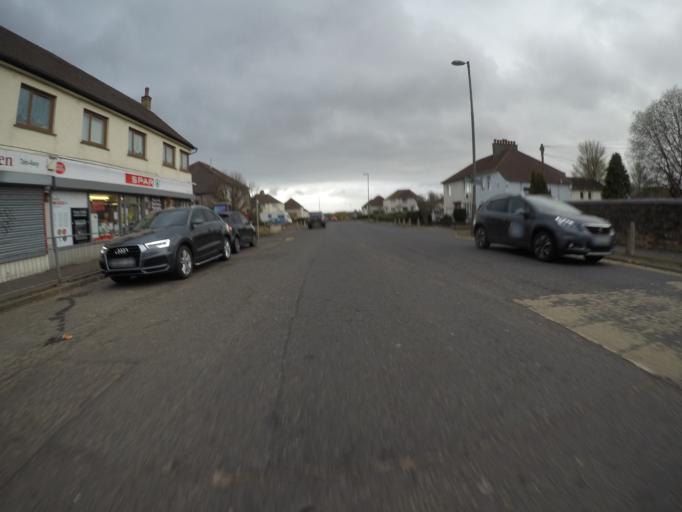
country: GB
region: Scotland
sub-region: East Ayrshire
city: Kilmarnock
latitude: 55.6126
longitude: -4.5154
